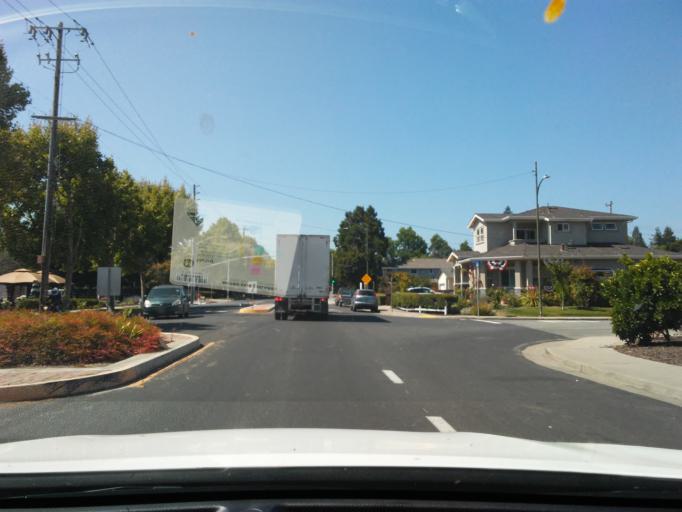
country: US
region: California
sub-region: Santa Clara County
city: Mountain View
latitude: 37.4014
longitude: -122.0581
